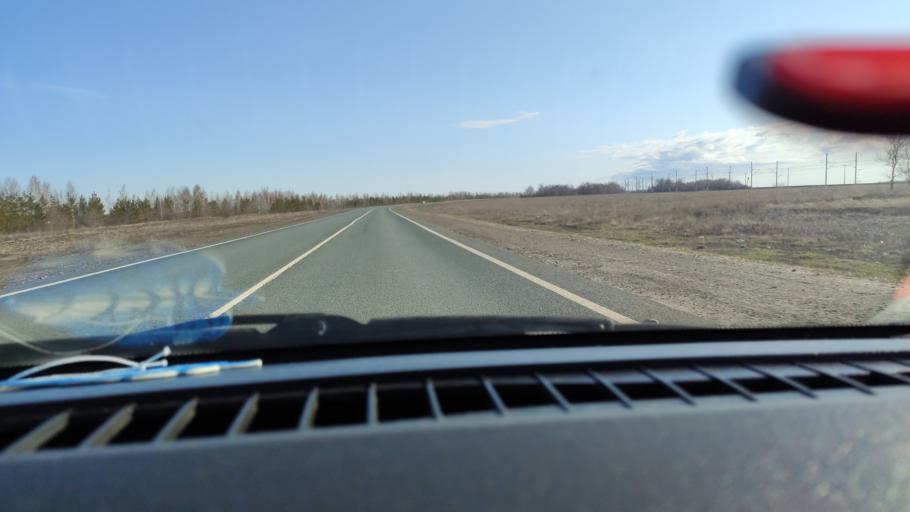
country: RU
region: Samara
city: Syzran'
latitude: 52.8605
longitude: 48.2645
